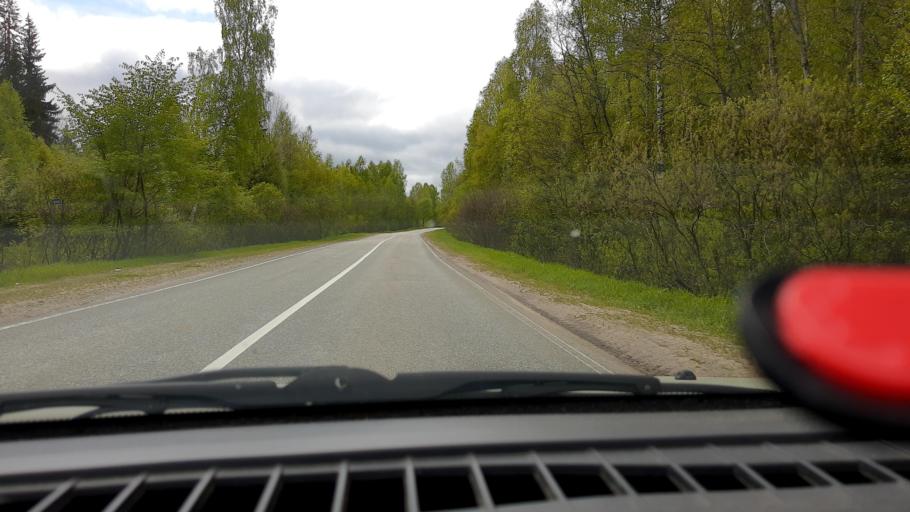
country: RU
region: Nizjnij Novgorod
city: Uren'
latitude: 57.2372
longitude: 45.5617
